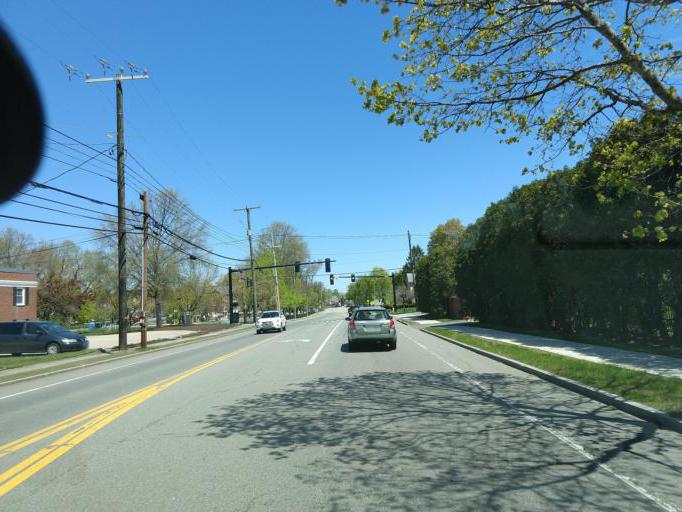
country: US
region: New Hampshire
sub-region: Rockingham County
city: Portsmouth
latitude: 43.0617
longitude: -70.7686
